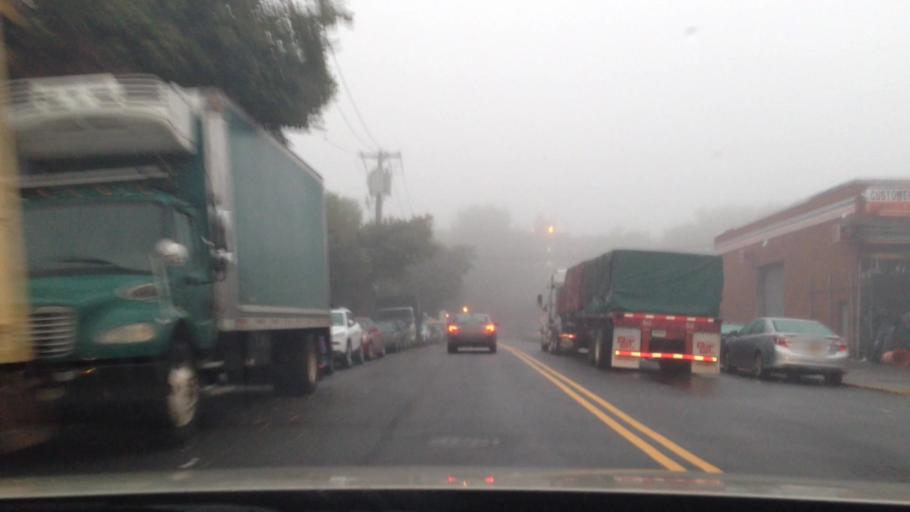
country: US
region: New York
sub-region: Kings County
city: Brooklyn
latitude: 40.6001
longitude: -73.9370
